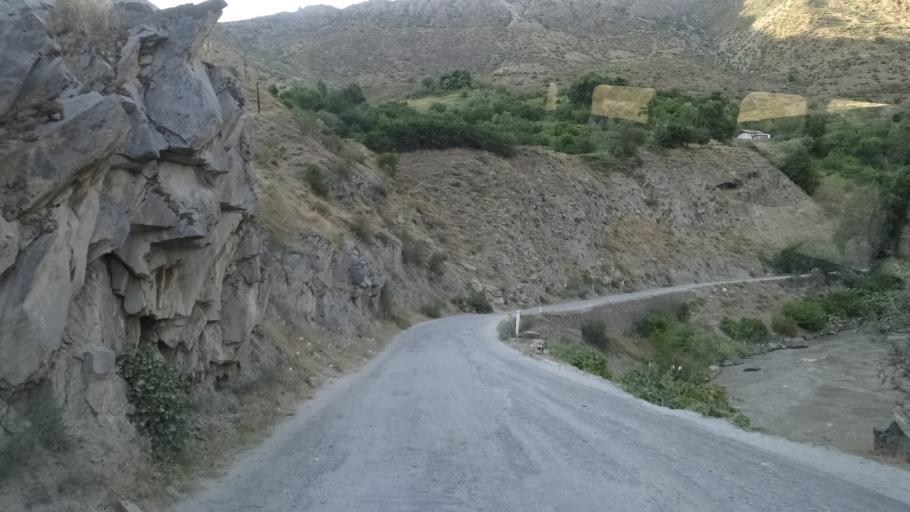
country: AF
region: Badakhshan
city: Maymay
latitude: 38.4913
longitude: 70.9875
